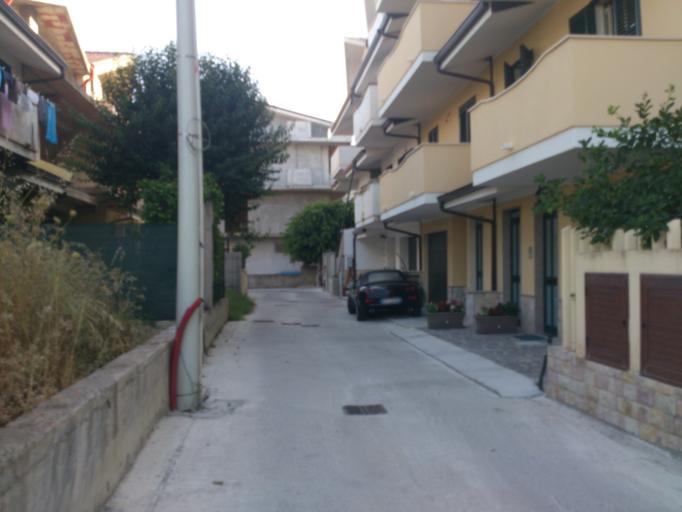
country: IT
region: Calabria
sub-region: Provincia di Reggio Calabria
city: Monasterace Marina
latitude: 38.4384
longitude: 16.5729
